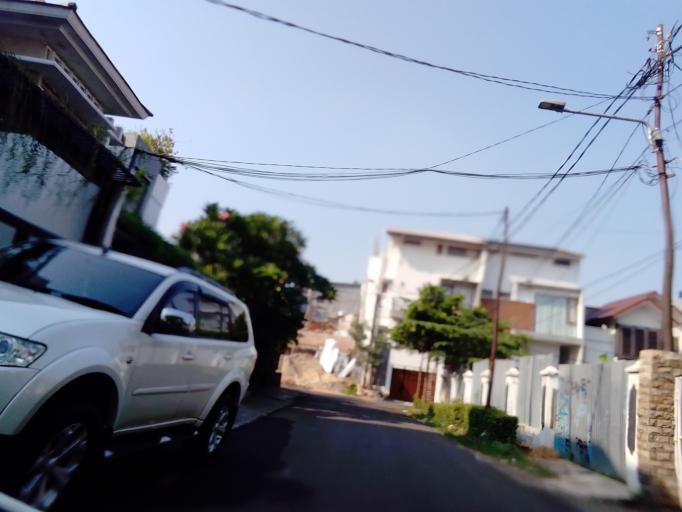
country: ID
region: Jakarta Raya
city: Jakarta
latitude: -6.2627
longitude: 106.8071
